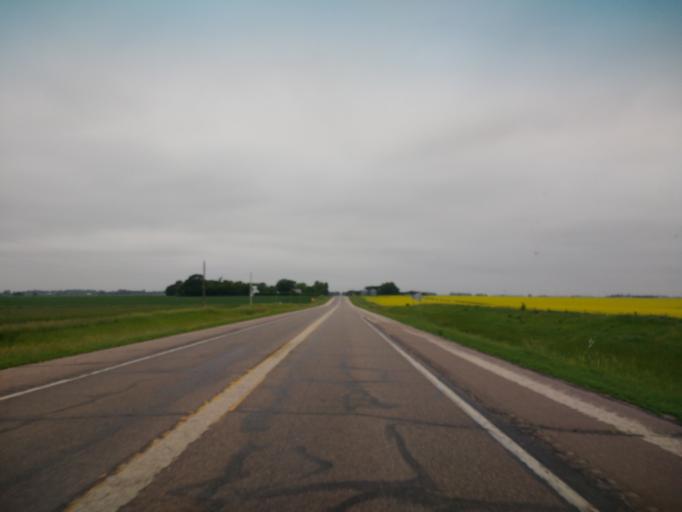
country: US
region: Iowa
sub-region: O'Brien County
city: Hartley
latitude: 43.1846
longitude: -95.4386
